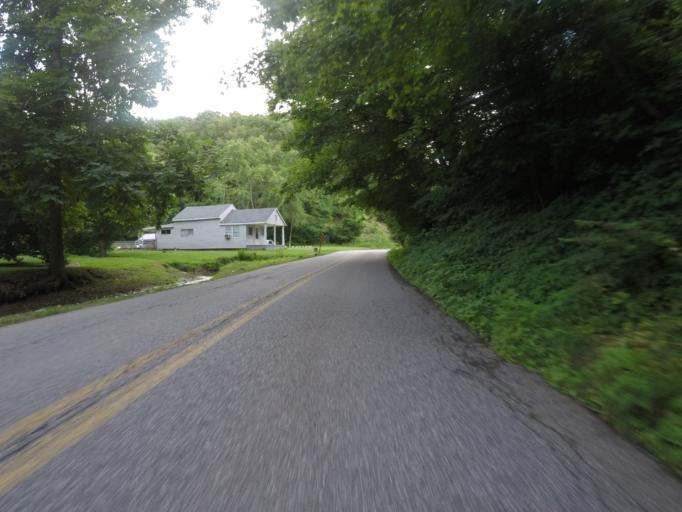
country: US
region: West Virginia
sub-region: Cabell County
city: Pea Ridge
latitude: 38.3984
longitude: -82.3619
